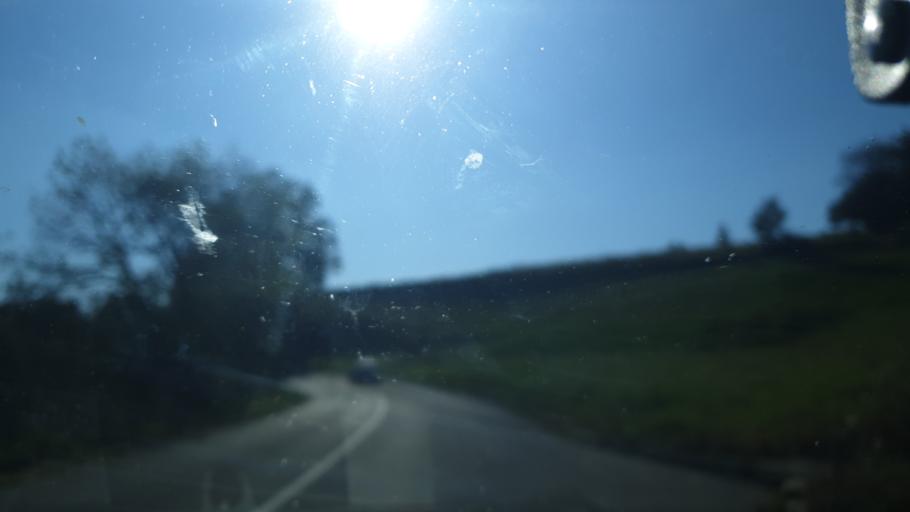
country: RS
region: Central Serbia
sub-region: Zlatiborski Okrug
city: Cajetina
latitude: 43.7158
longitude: 19.7747
